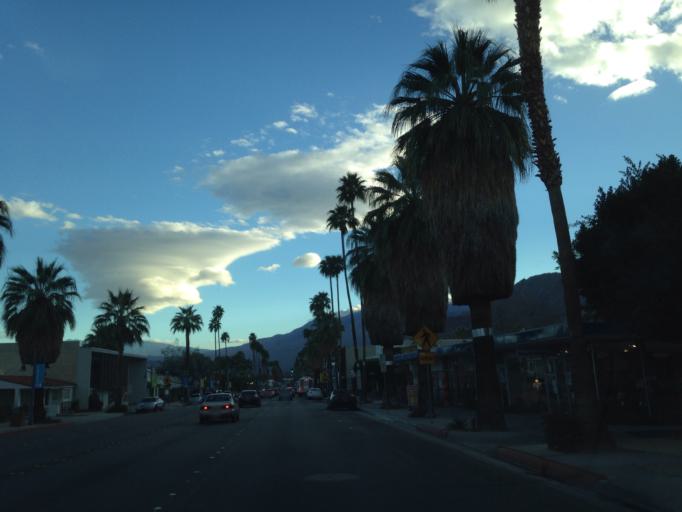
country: US
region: California
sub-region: Riverside County
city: Palm Springs
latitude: 33.8337
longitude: -116.5469
